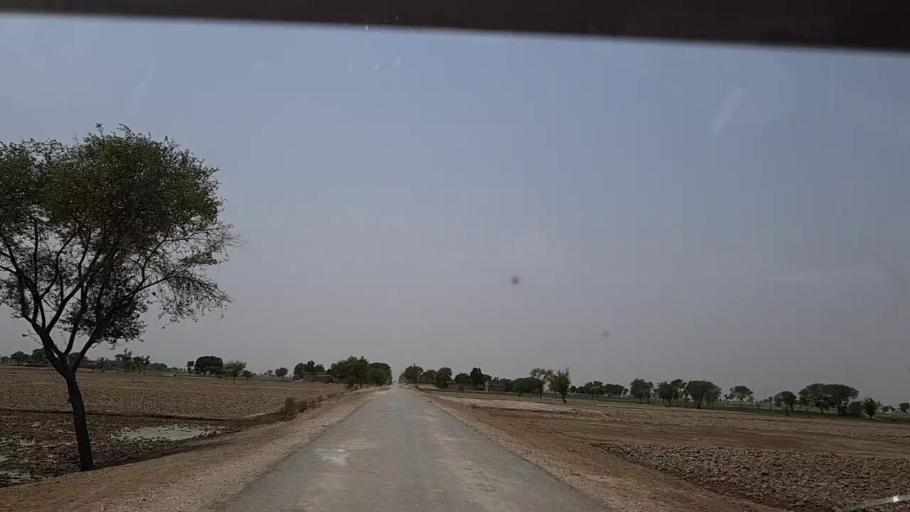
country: PK
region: Sindh
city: Phulji
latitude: 27.0059
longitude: 67.6349
